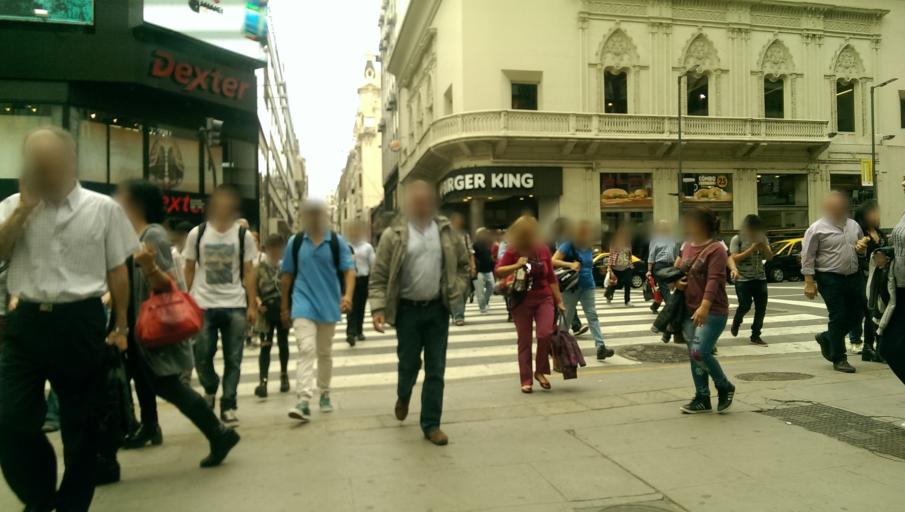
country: AR
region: Buenos Aires F.D.
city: Buenos Aires
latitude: -34.6033
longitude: -58.3753
